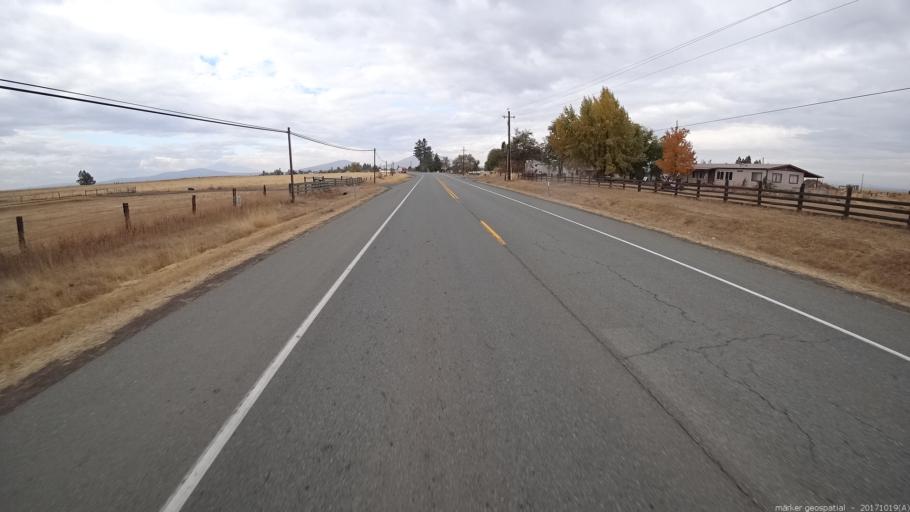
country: US
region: California
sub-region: Shasta County
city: Burney
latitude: 41.0555
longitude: -121.3865
